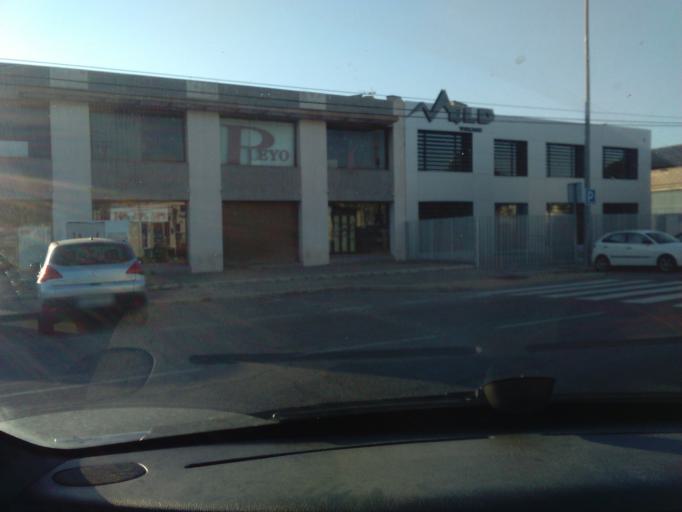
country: ES
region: Andalusia
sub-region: Provincia de Sevilla
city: Sevilla
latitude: 37.3950
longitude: -5.9470
